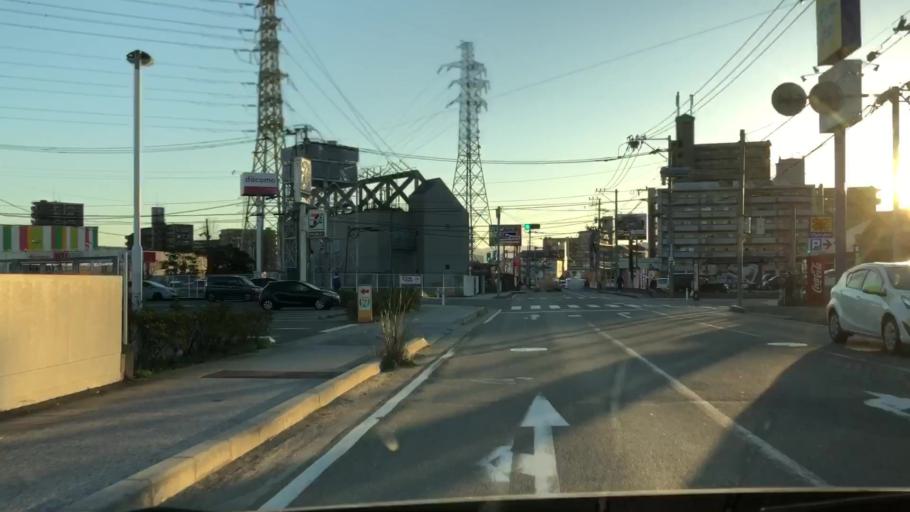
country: JP
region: Fukuoka
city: Fukuoka-shi
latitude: 33.6238
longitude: 130.4386
